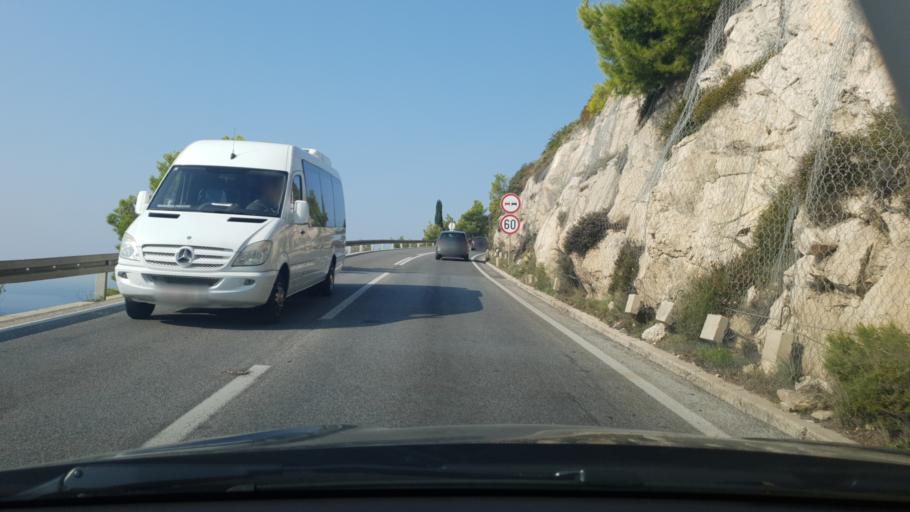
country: HR
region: Dubrovacko-Neretvanska
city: Cibaca
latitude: 42.6318
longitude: 18.1465
